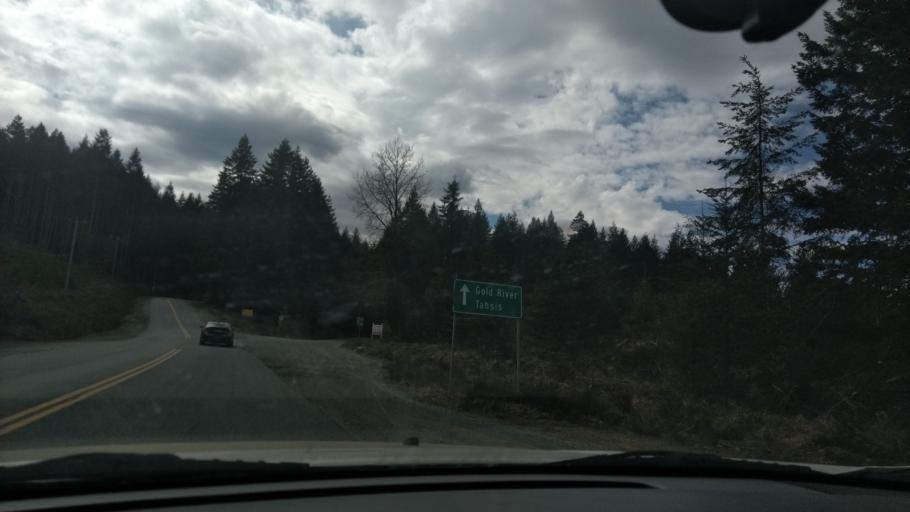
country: CA
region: British Columbia
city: Campbell River
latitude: 49.9855
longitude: -125.4251
